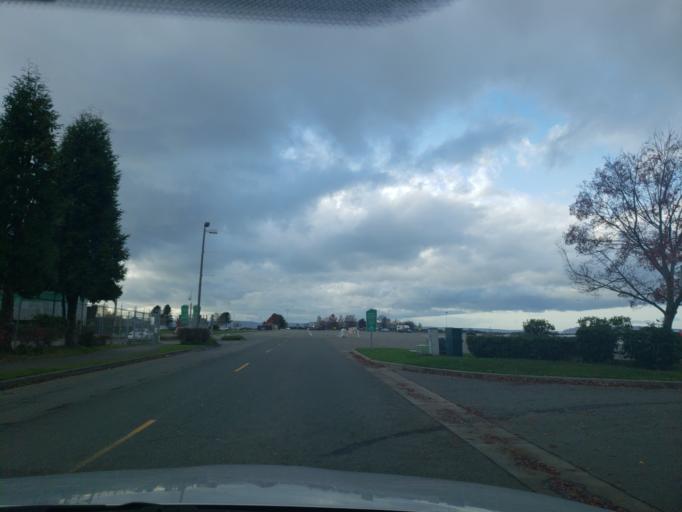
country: US
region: Washington
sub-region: Snohomish County
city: Everett
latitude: 48.0043
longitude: -122.2169
